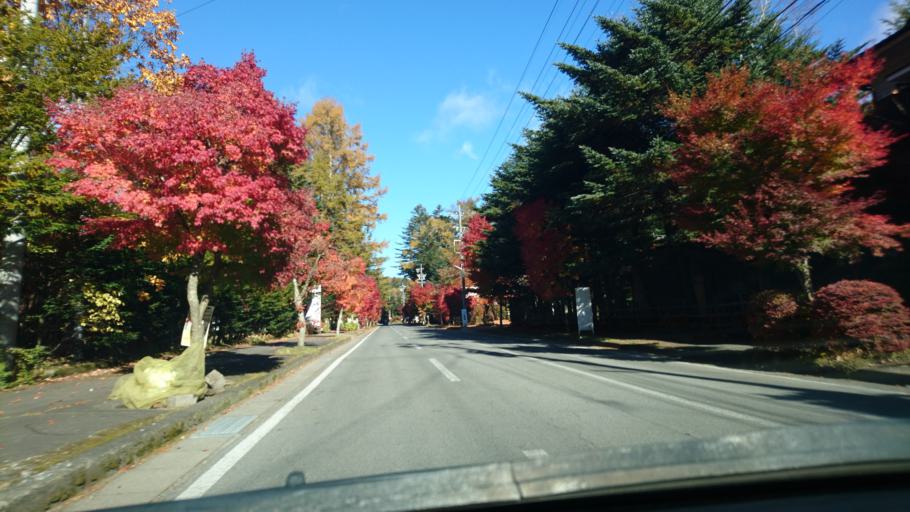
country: JP
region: Nagano
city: Komoro
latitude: 36.3596
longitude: 138.6330
